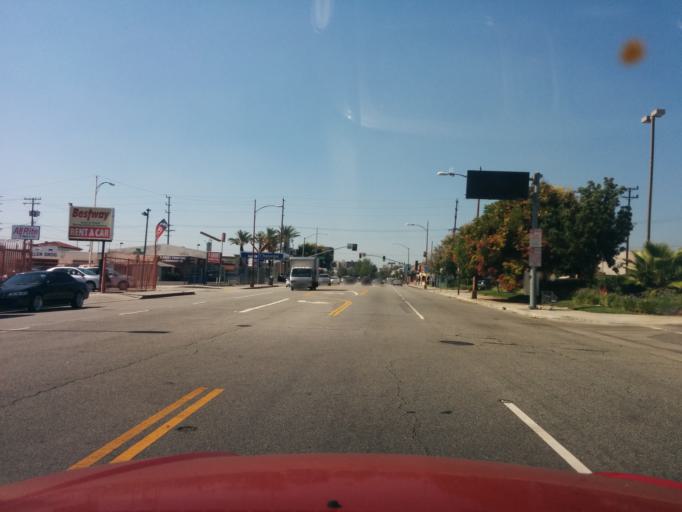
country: US
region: California
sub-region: Los Angeles County
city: Burbank
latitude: 34.1737
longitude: -118.2987
